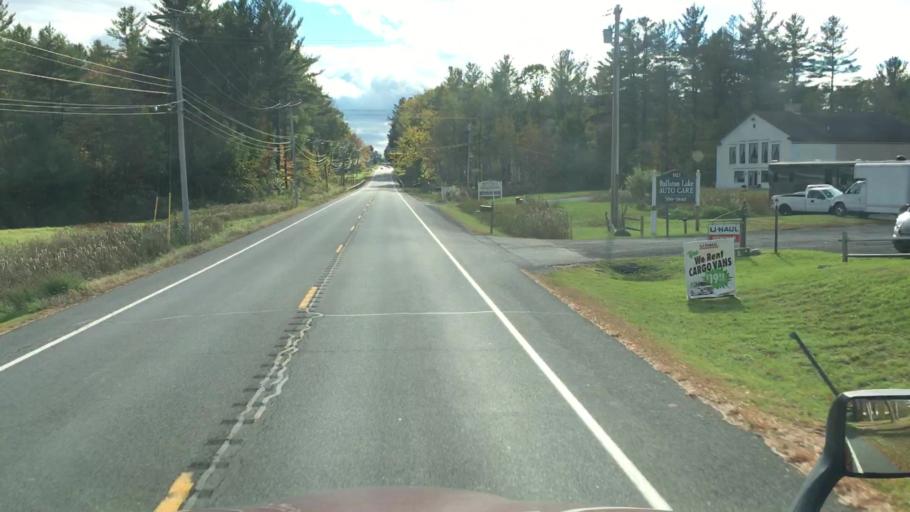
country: US
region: New York
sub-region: Saratoga County
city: Ballston Spa
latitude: 42.9437
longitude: -73.8709
